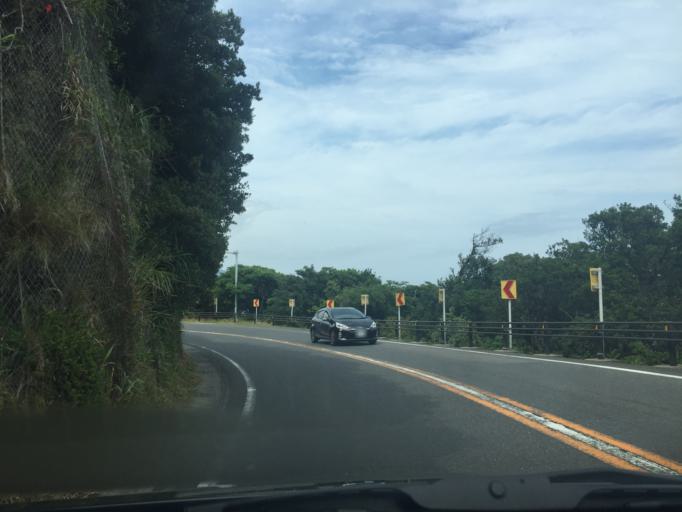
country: JP
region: Shizuoka
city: Shimoda
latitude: 34.7171
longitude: 138.9910
